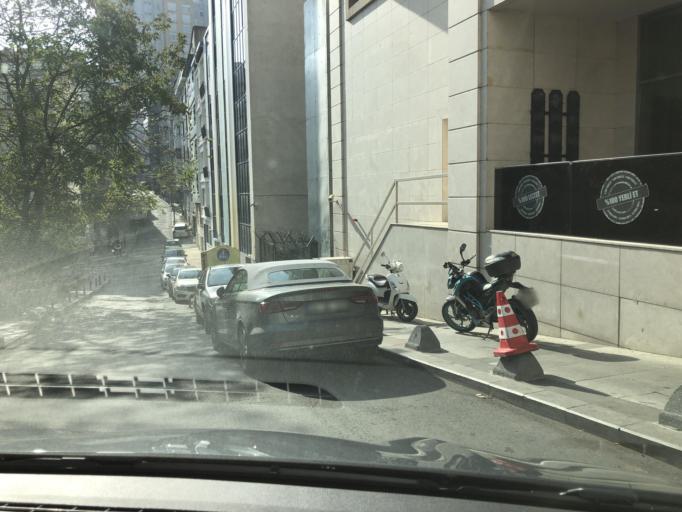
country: TR
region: Istanbul
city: Sisli
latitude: 41.0609
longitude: 28.9893
